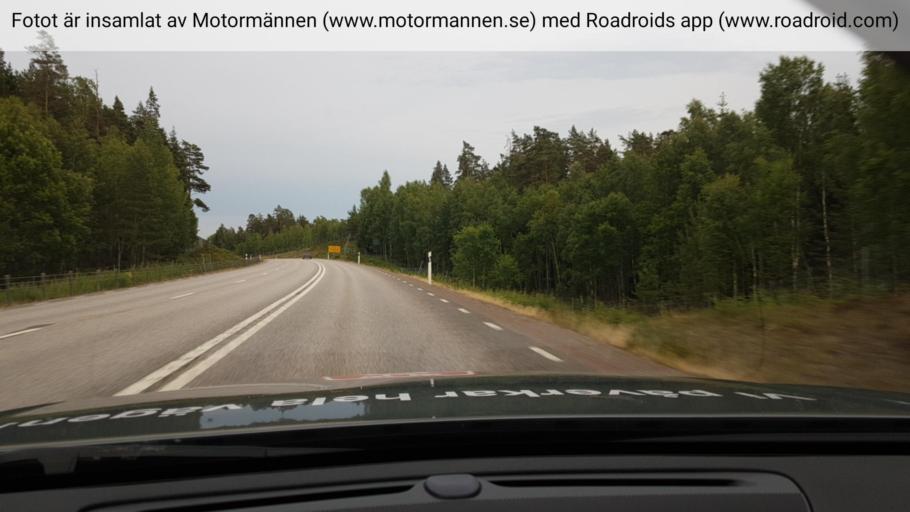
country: SE
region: OEstergoetland
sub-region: Motala Kommun
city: Borensberg
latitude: 58.5666
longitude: 15.3034
